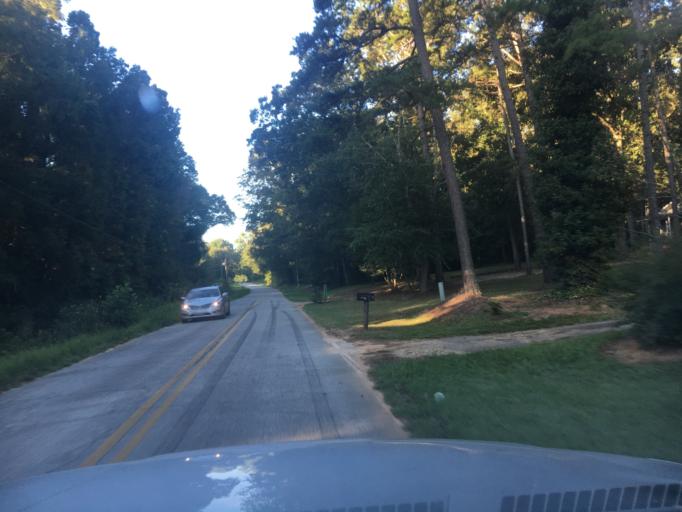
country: US
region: South Carolina
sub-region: Spartanburg County
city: Woodruff
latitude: 34.6663
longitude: -81.9643
